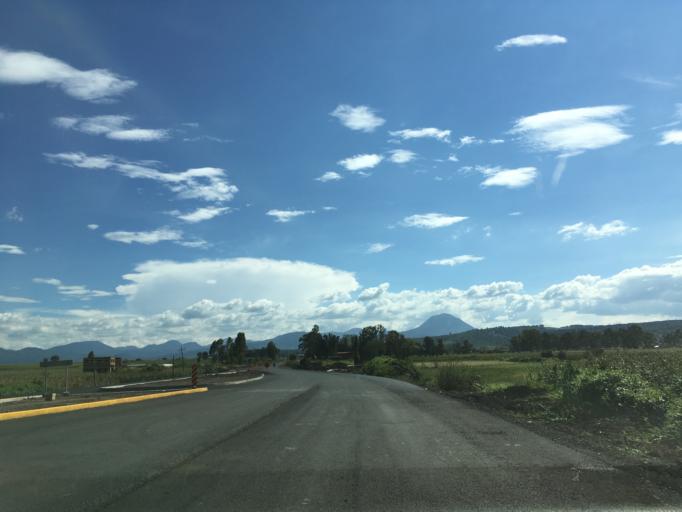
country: MX
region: Michoacan
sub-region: Jimenez
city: Villa Jimenez
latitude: 19.9022
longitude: -101.7650
